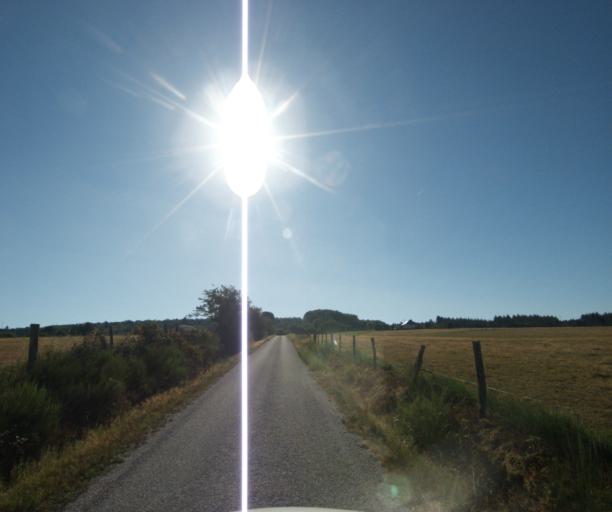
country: FR
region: Lorraine
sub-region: Departement des Vosges
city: Epinal
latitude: 48.1746
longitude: 6.4753
